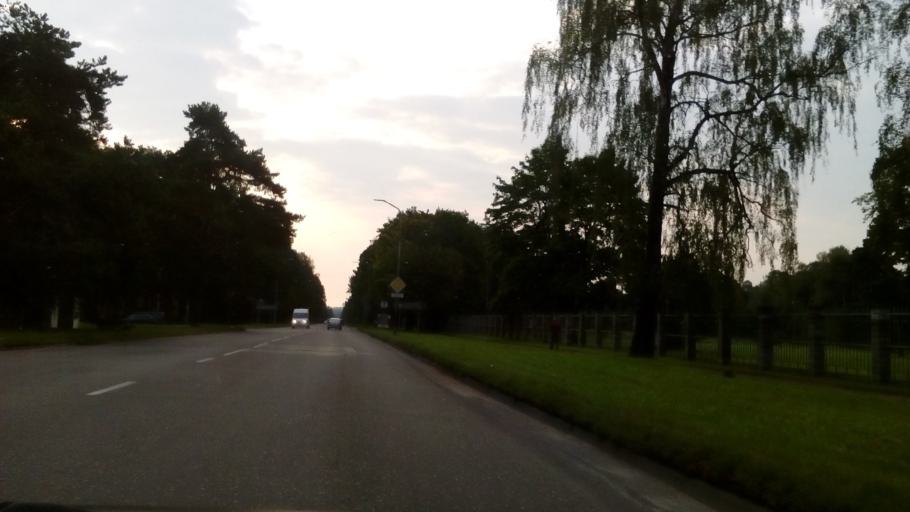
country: LT
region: Alytaus apskritis
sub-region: Alytus
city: Alytus
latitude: 54.3820
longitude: 24.0562
